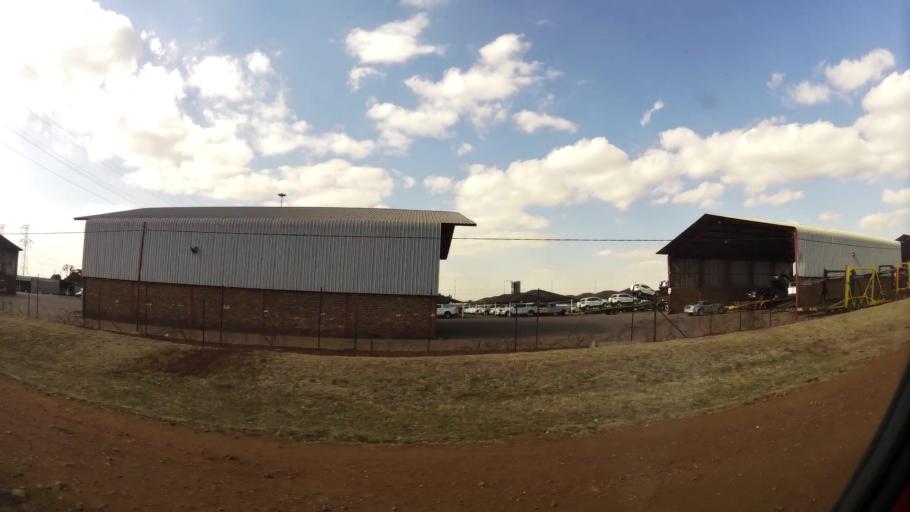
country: ZA
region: Gauteng
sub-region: Ekurhuleni Metropolitan Municipality
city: Tembisa
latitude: -26.0165
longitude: 28.2553
